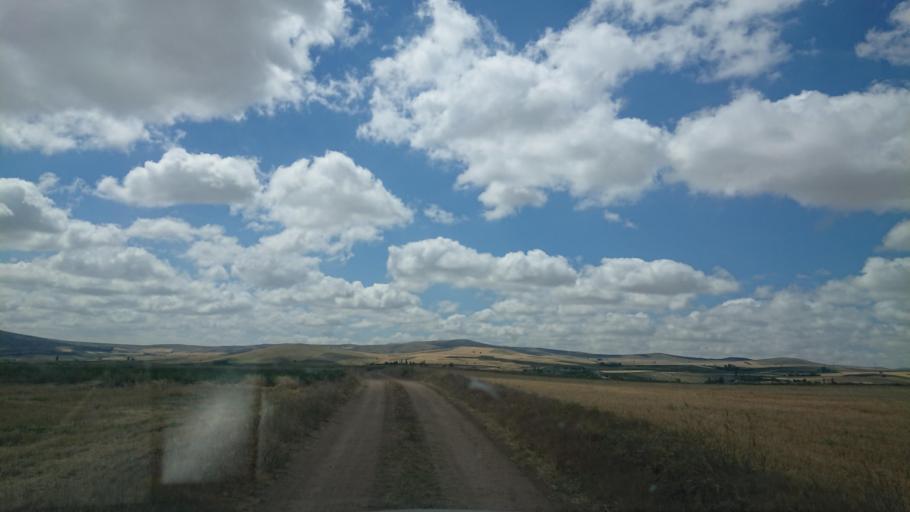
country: TR
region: Aksaray
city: Agacoren
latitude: 38.8298
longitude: 33.9526
